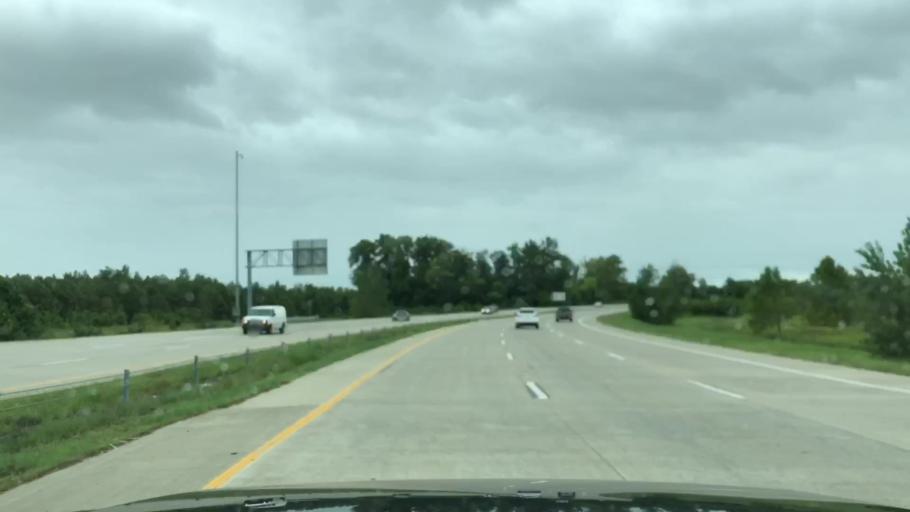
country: US
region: Missouri
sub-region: Saint Louis County
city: Maryland Heights
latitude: 38.6956
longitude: -90.5018
